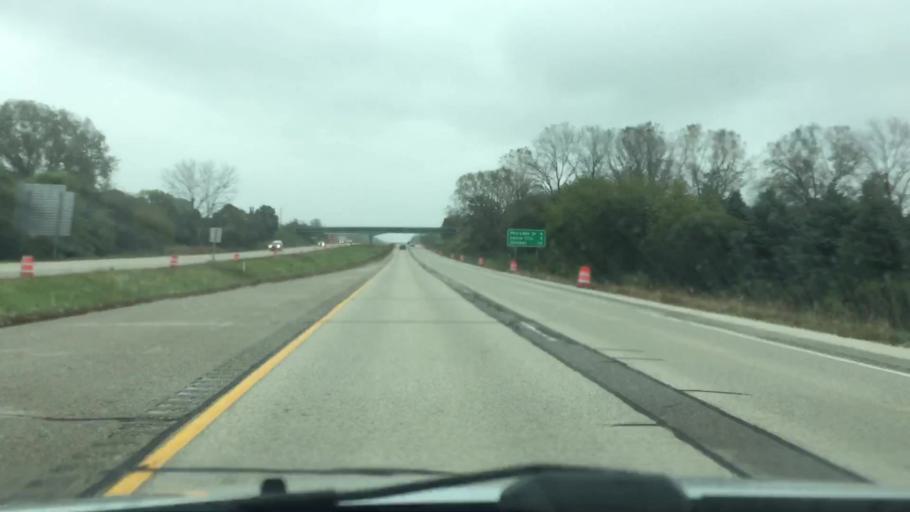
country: US
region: Wisconsin
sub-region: Walworth County
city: Lake Geneva
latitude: 42.5831
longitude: -88.3960
